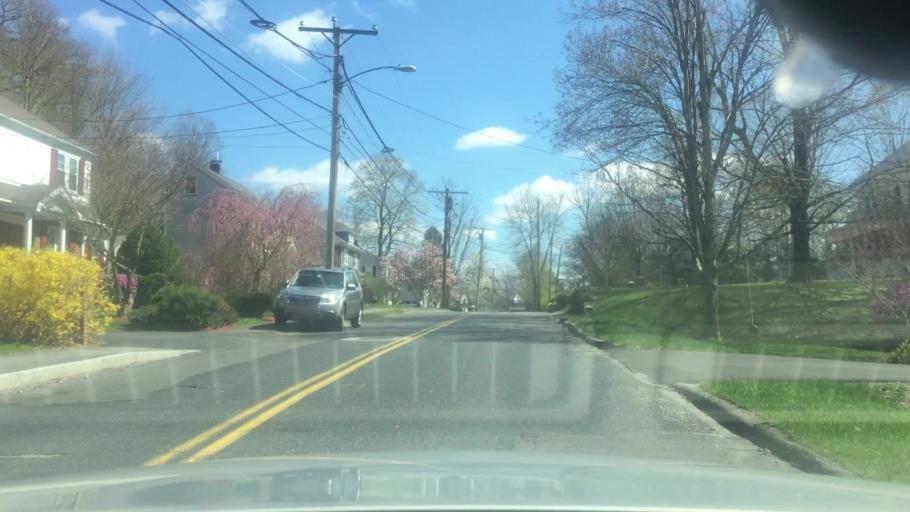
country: US
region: Massachusetts
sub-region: Norfolk County
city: Needham
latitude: 42.2826
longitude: -71.2408
